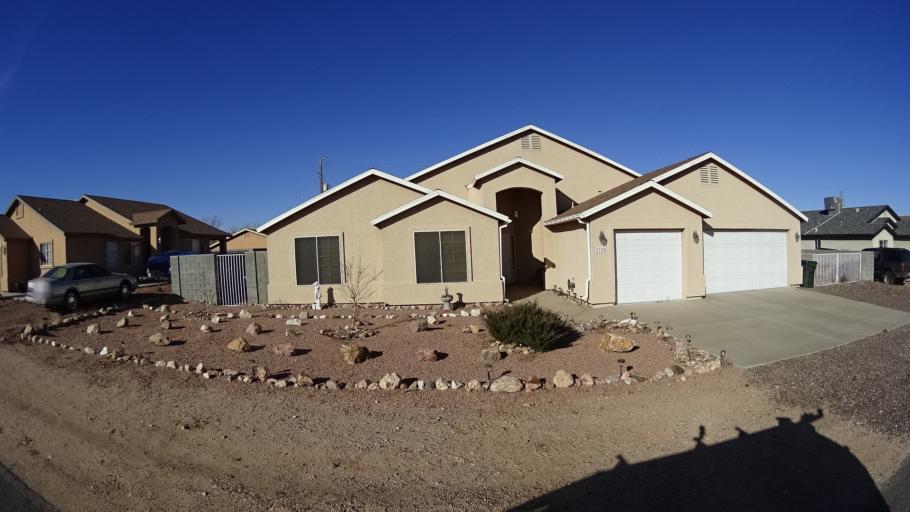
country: US
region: Arizona
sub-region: Mohave County
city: Kingman
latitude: 35.2111
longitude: -114.0027
